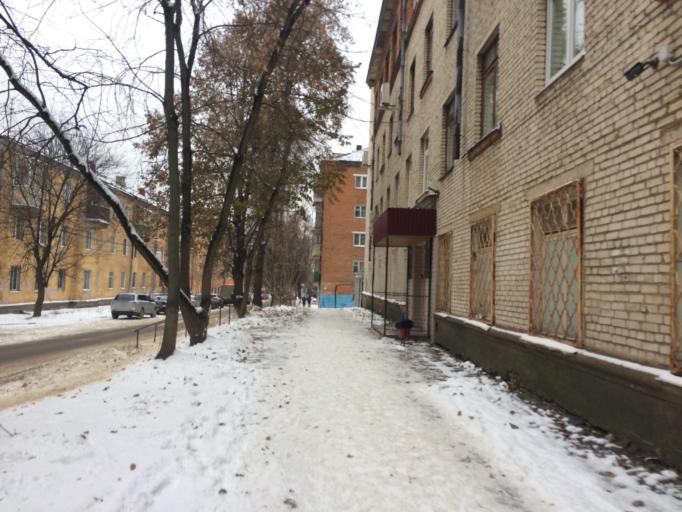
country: RU
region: Tula
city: Mendeleyevskiy
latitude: 54.1690
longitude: 37.5876
